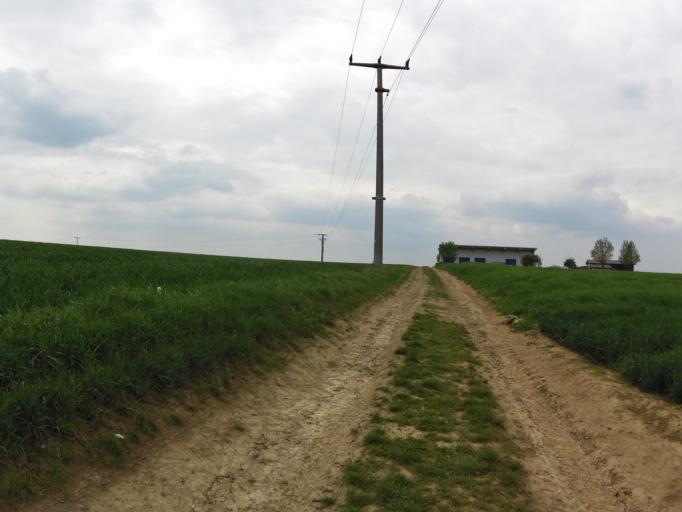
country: DE
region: Bavaria
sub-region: Regierungsbezirk Unterfranken
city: Unterpleichfeld
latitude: 49.8628
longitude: 10.0495
